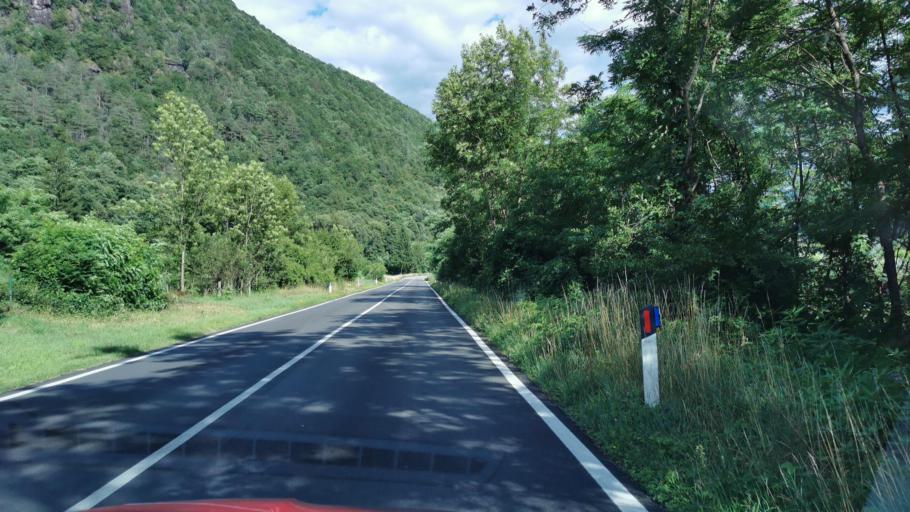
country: IT
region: Lombardy
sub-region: Provincia di Lecco
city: Cortenova
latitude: 45.9996
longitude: 9.3907
